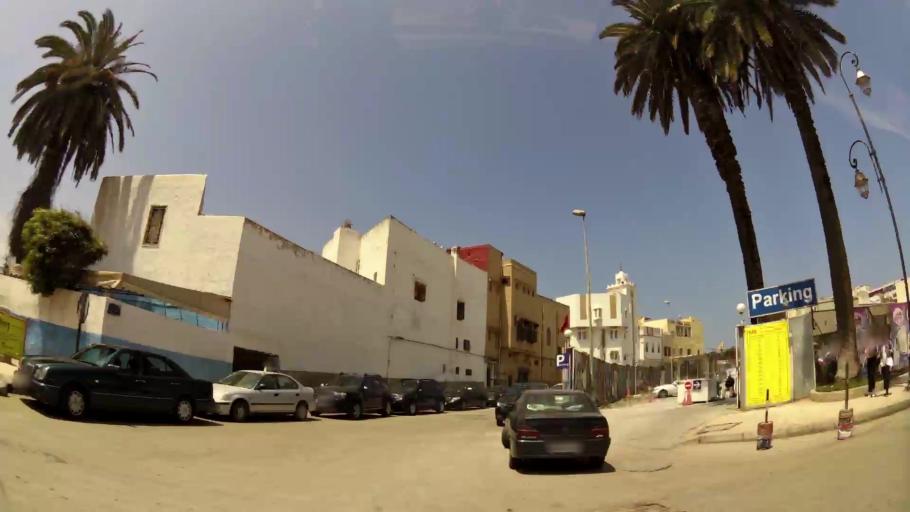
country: MA
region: Rabat-Sale-Zemmour-Zaer
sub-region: Rabat
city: Rabat
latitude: 34.0238
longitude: -6.8411
